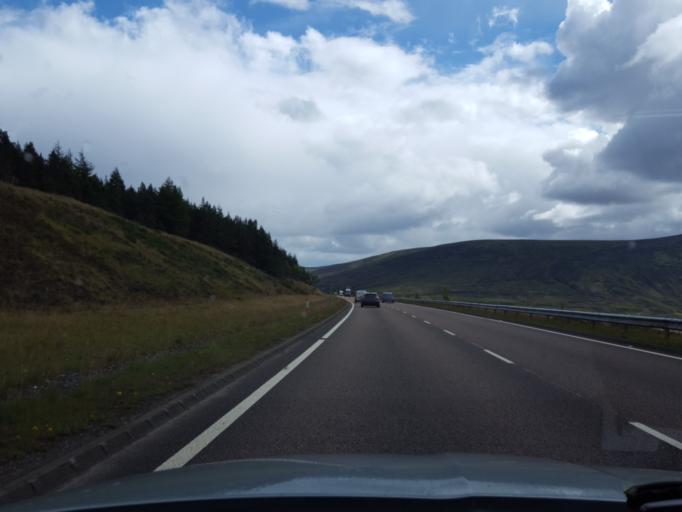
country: GB
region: Scotland
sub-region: Highland
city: Kingussie
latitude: 56.8385
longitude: -4.2330
